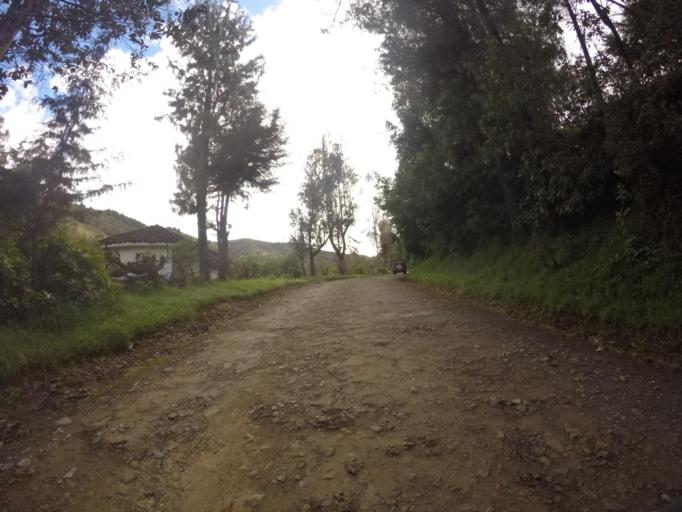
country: CO
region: Cauca
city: Silvia
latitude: 2.6618
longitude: -76.3580
